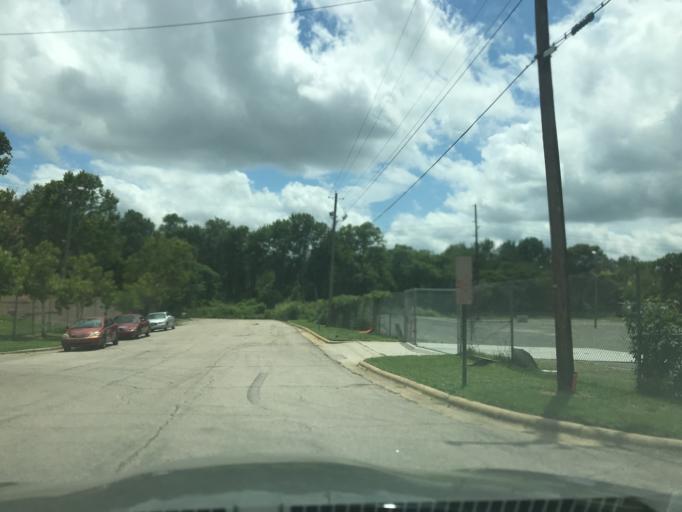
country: US
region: North Carolina
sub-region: Wake County
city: Raleigh
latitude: 35.8157
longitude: -78.6213
